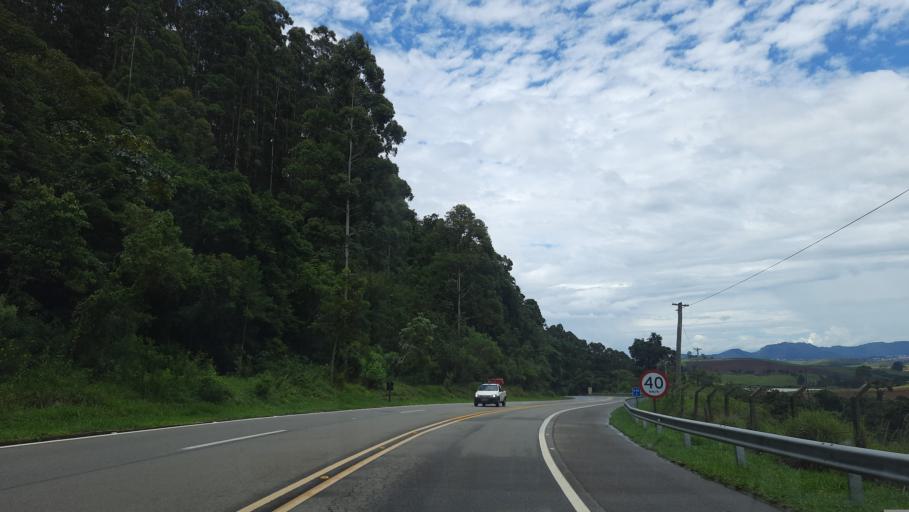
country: BR
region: Minas Gerais
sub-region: Pocos De Caldas
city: Pocos de Caldas
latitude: -21.8455
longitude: -46.6885
